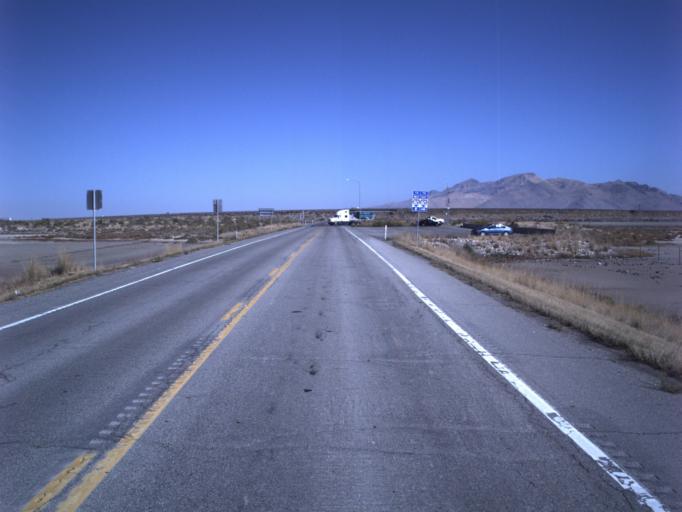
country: US
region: Utah
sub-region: Tooele County
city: Grantsville
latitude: 40.7027
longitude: -112.5299
